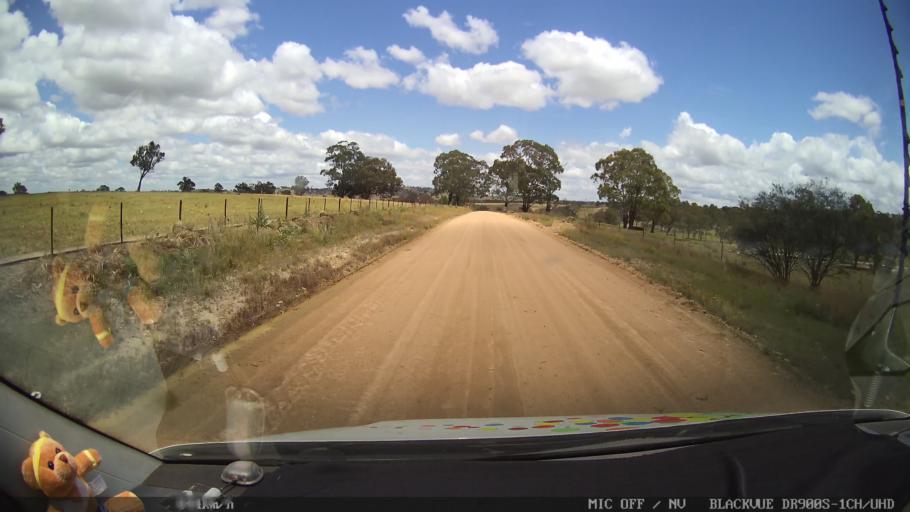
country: AU
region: New South Wales
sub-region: Glen Innes Severn
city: Glen Innes
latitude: -29.3492
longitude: 151.8860
